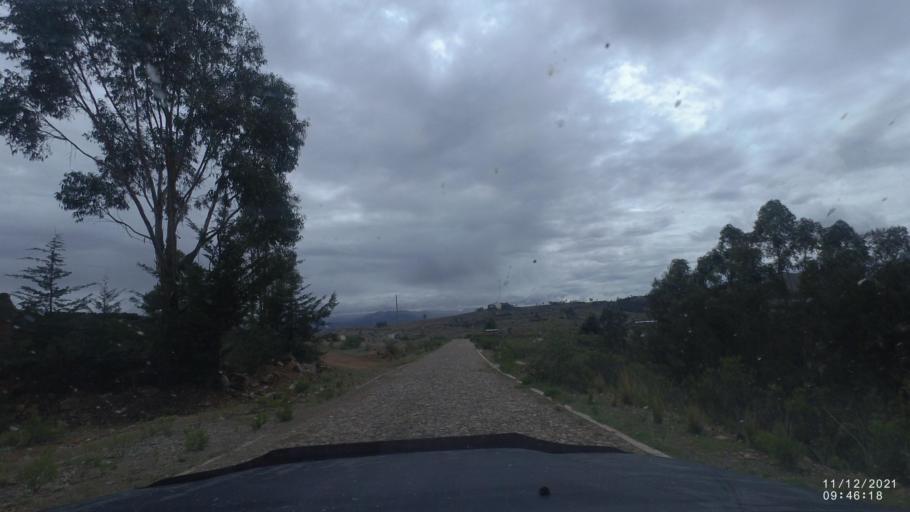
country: BO
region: Cochabamba
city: Tarata
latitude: -17.7876
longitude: -65.9727
